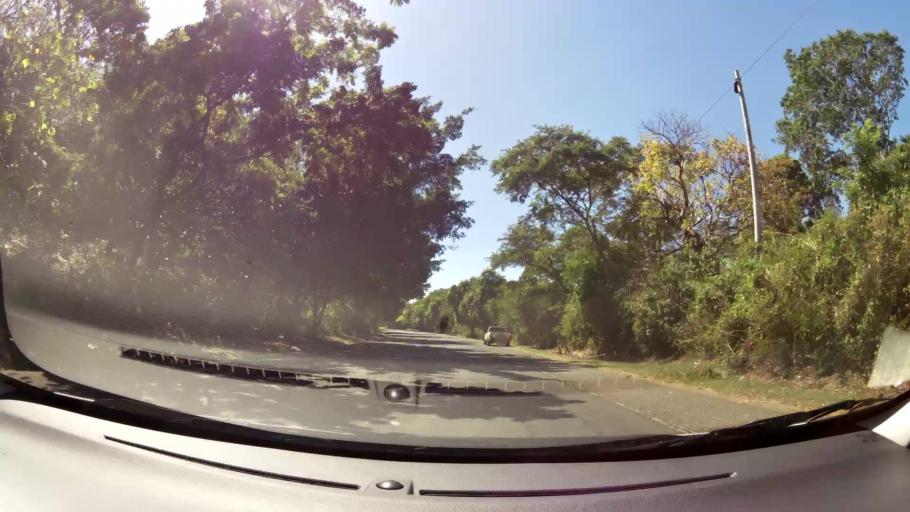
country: SV
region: Ahuachapan
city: Ahuachapan
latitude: 13.9498
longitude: -89.8381
